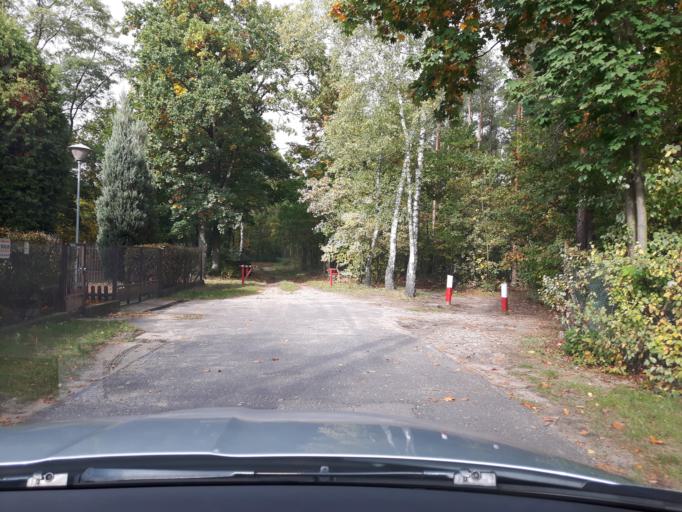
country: PL
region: Masovian Voivodeship
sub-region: Powiat wolominski
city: Zabki
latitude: 52.2995
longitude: 21.1237
